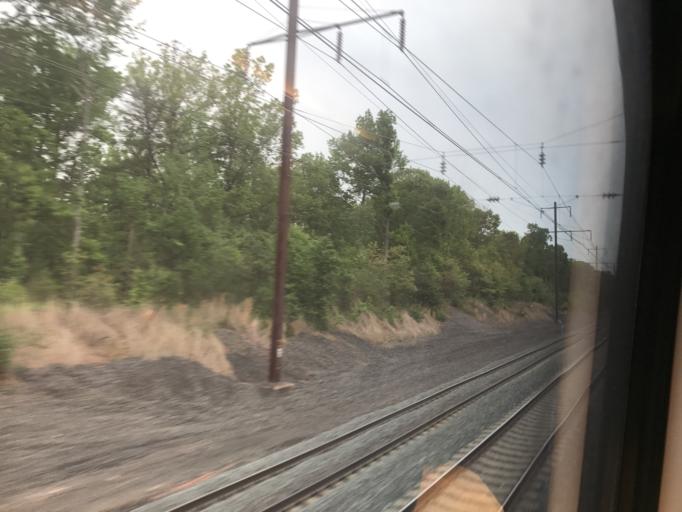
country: US
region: Maryland
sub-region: Prince George's County
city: Glenn Dale
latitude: 38.9920
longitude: -76.8073
